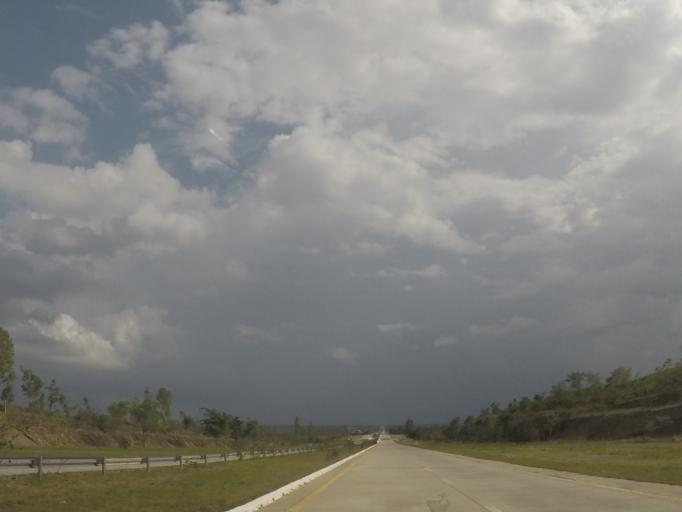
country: MM
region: Mandalay
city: Meiktila
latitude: 21.1386
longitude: 95.8019
